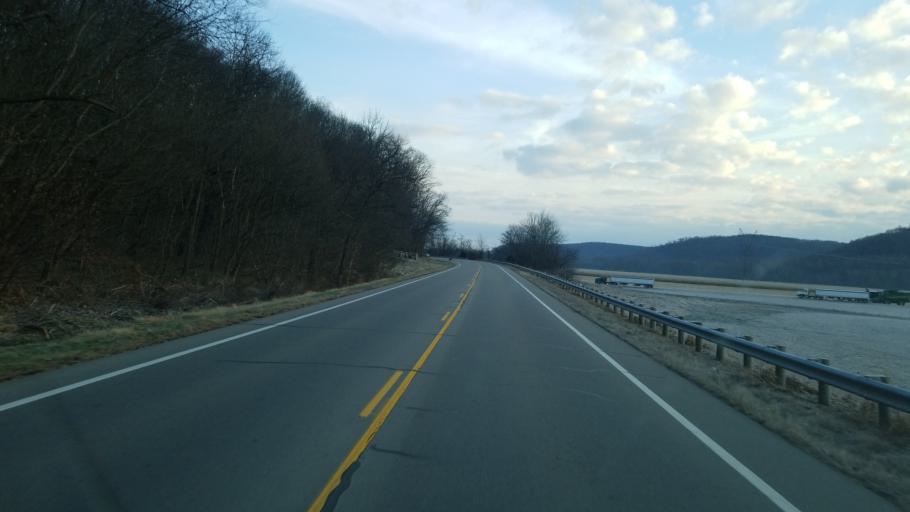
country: US
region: Ohio
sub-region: Ross County
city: North Fork Village
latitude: 39.3179
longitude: -83.1064
